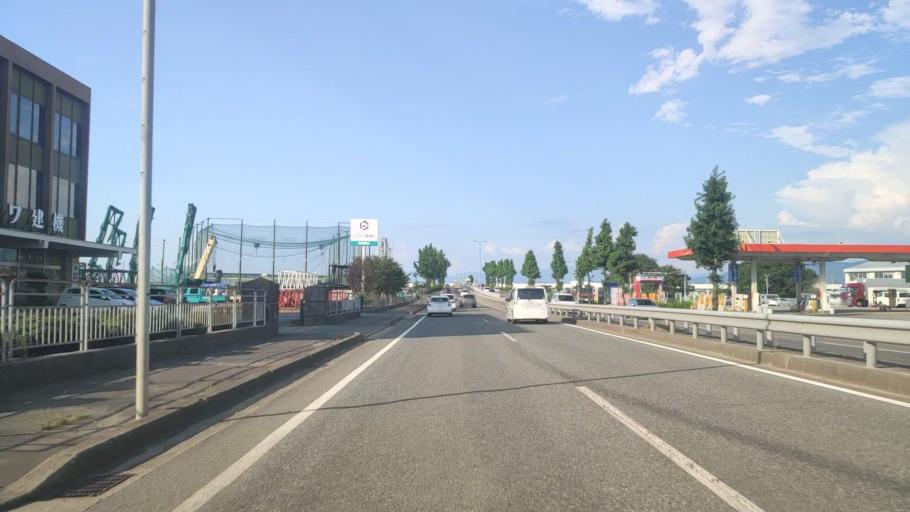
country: JP
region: Fukui
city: Fukui-shi
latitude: 36.0219
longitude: 136.2155
